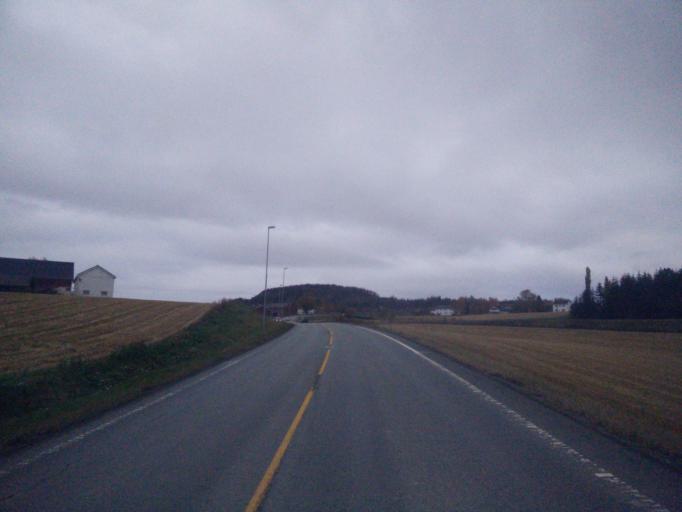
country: NO
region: Nord-Trondelag
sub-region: Stjordal
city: Stjordal
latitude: 63.5012
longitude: 10.8631
